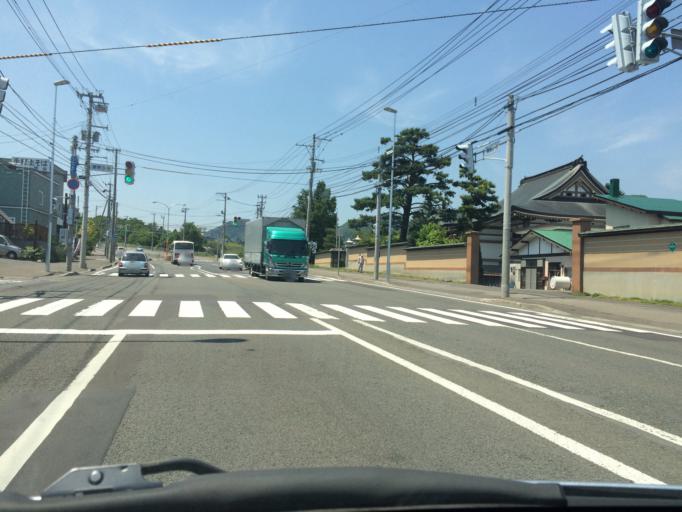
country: JP
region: Hokkaido
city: Sapporo
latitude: 42.9620
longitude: 141.2881
